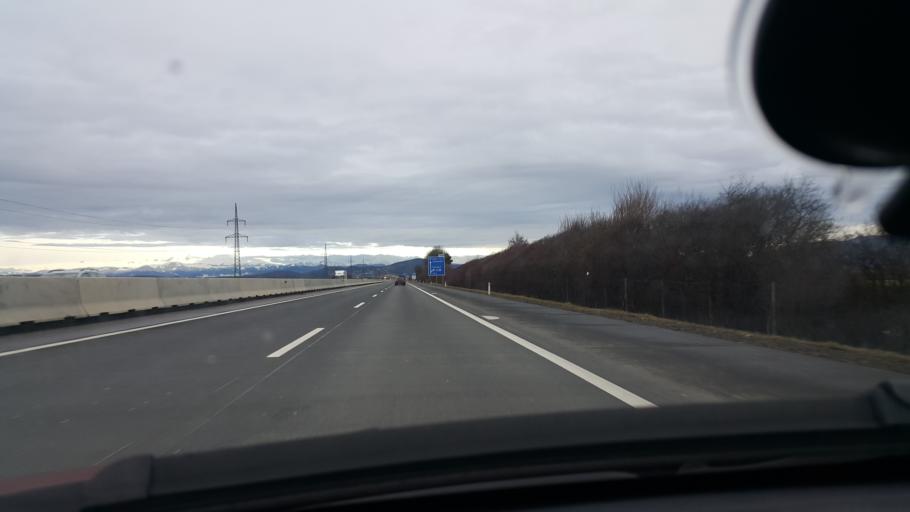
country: AT
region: Styria
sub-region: Politischer Bezirk Graz-Umgebung
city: Wundschuh
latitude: 46.9521
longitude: 15.4471
